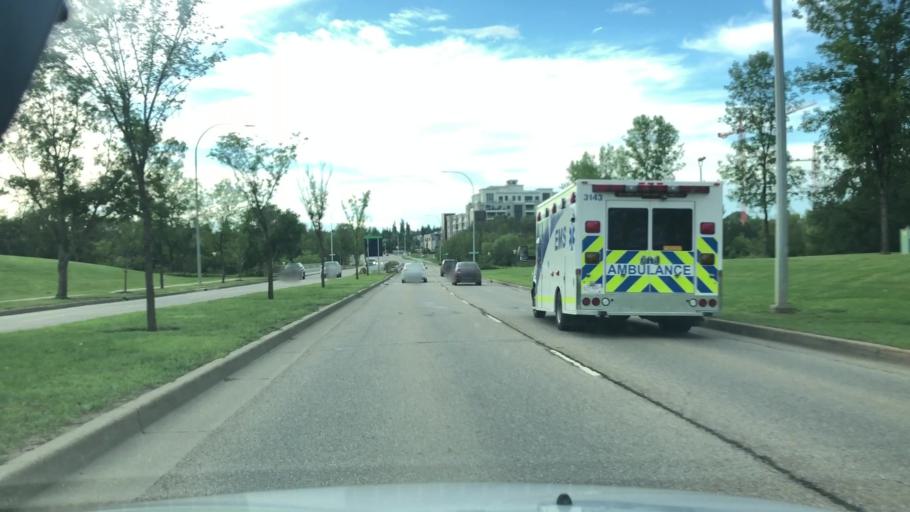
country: CA
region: Alberta
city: St. Albert
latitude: 53.6465
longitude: -113.6124
